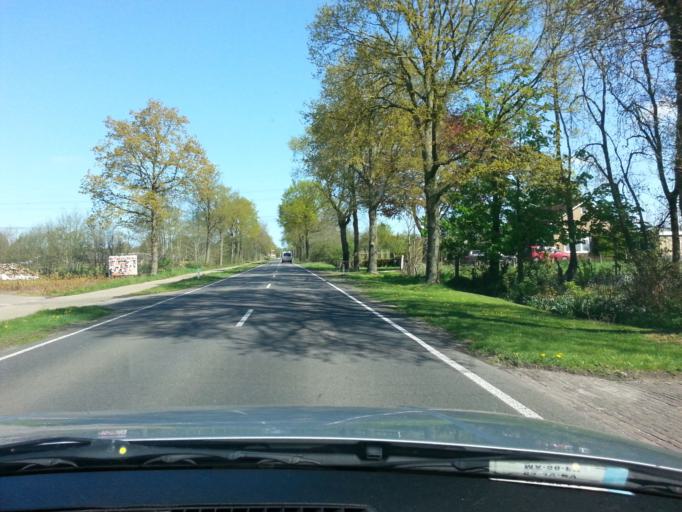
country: NL
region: Friesland
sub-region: Gemeente Achtkarspelen
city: Surhuizum
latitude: 53.1932
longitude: 6.1855
